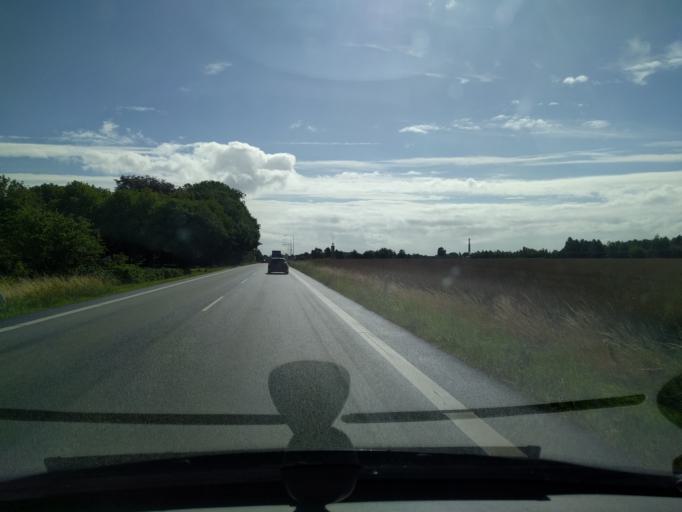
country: DK
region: South Denmark
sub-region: Kerteminde Kommune
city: Langeskov
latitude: 55.3648
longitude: 10.5801
